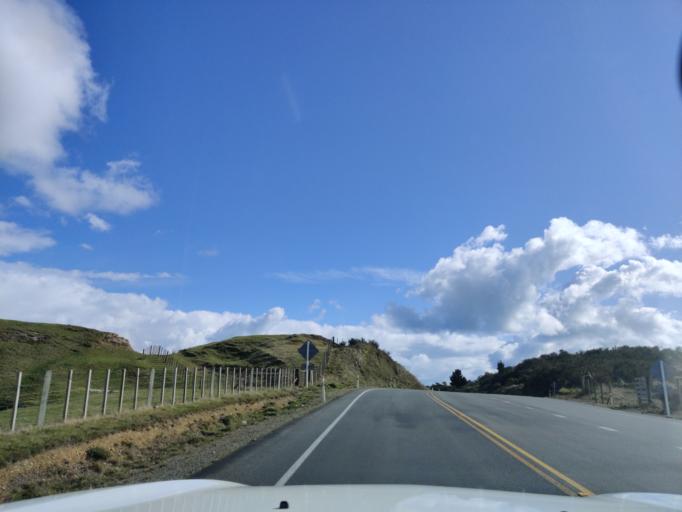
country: NZ
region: Manawatu-Wanganui
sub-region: Palmerston North City
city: Palmerston North
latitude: -40.2910
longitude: 175.8023
